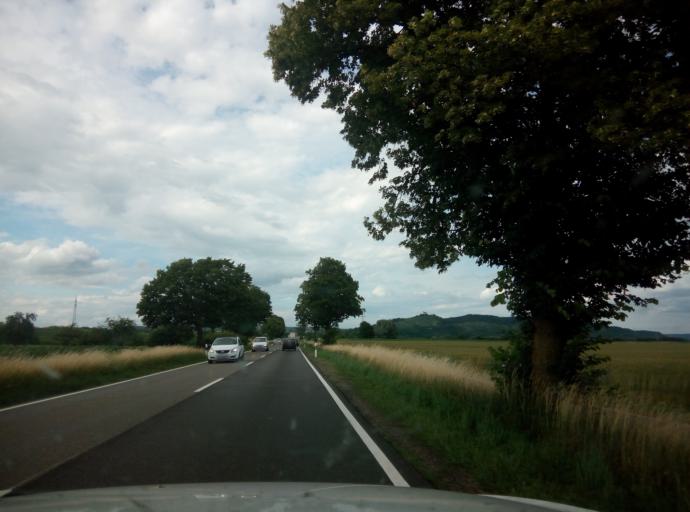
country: DE
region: Baden-Wuerttemberg
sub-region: Tuebingen Region
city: Rottenburg
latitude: 48.4910
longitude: 8.9538
